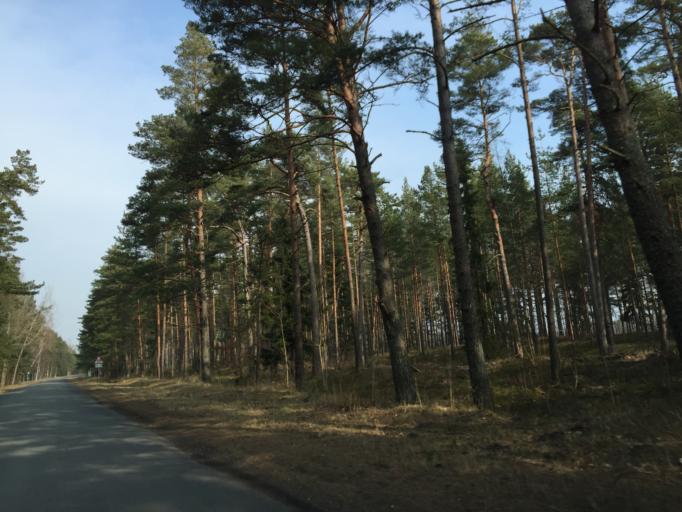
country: LV
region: Salacgrivas
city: Ainazi
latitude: 57.9020
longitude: 24.3769
